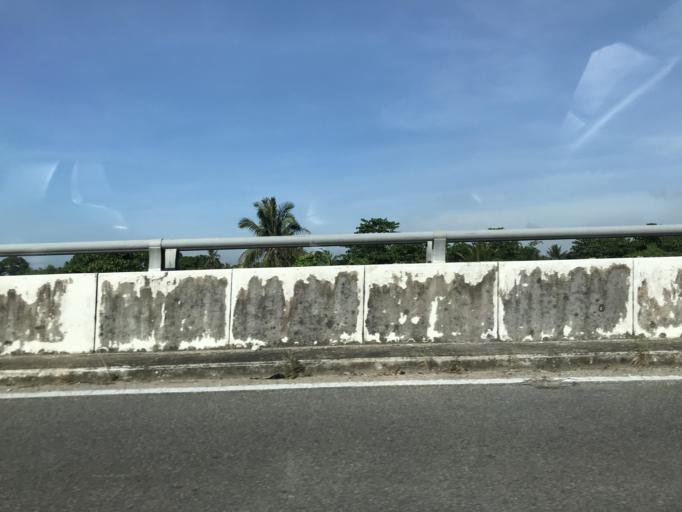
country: MY
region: Kelantan
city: Kampong Kadok
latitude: 6.0545
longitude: 102.2149
